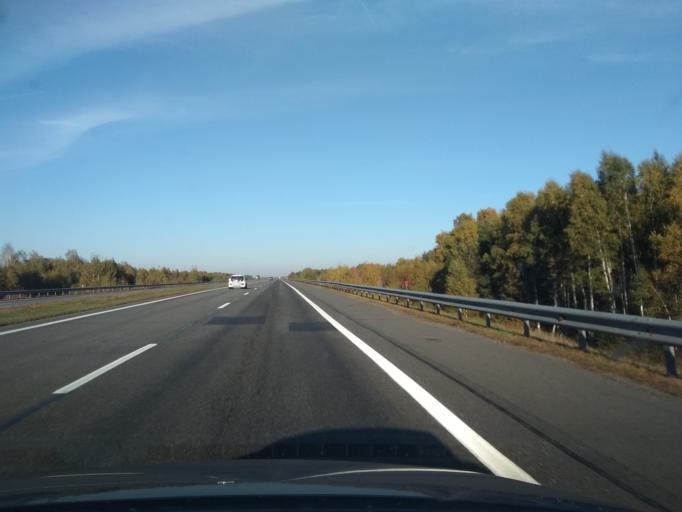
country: BY
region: Brest
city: Nyakhachava
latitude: 52.5936
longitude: 25.1464
